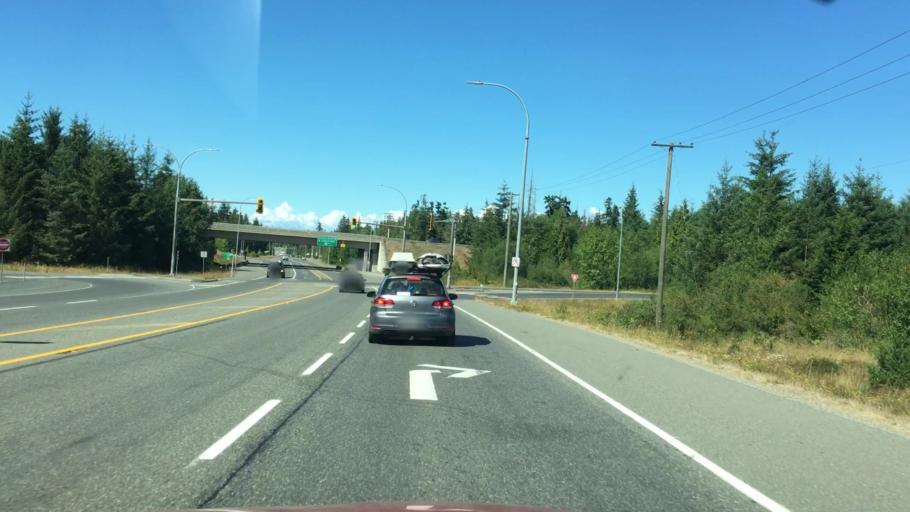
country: CA
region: British Columbia
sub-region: Regional District of Nanaimo
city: Parksville
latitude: 49.3229
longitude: -124.4414
